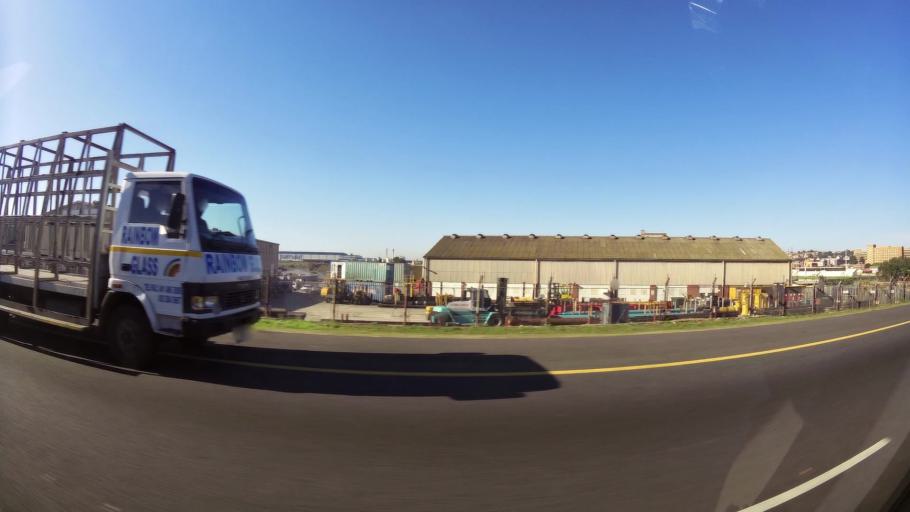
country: ZA
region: Eastern Cape
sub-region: Nelson Mandela Bay Metropolitan Municipality
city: Port Elizabeth
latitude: -33.9186
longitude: 25.5732
